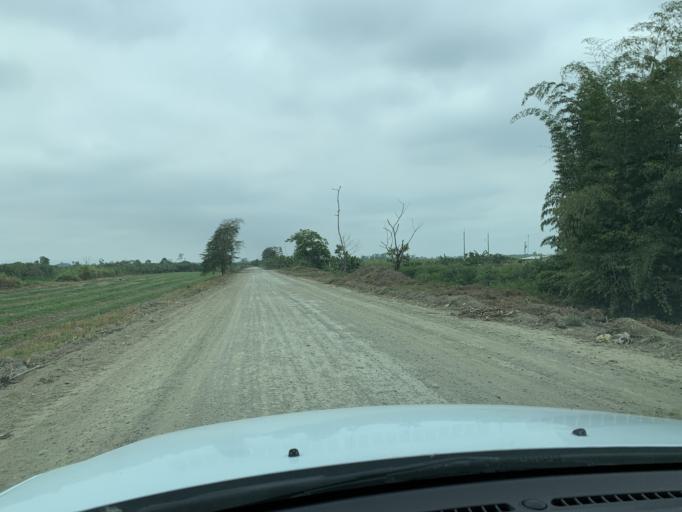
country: EC
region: Canar
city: La Troncal
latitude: -2.3697
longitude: -79.4415
